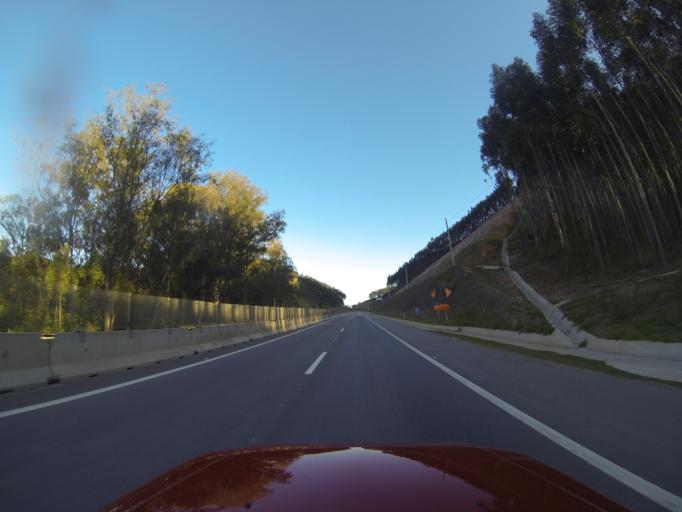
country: BR
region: Sao Paulo
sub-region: Santa Branca
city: Santa Branca
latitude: -23.3305
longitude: -45.7153
